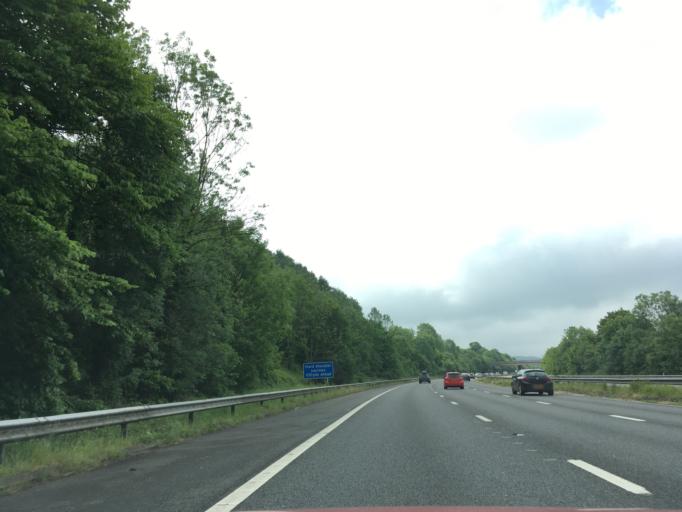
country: GB
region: England
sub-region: Devon
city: Cullompton
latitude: 50.8401
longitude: -3.3899
